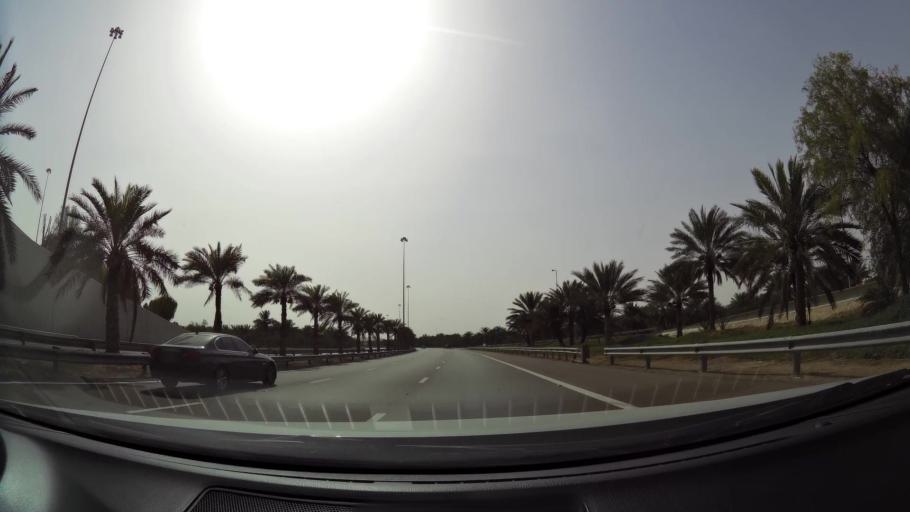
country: AE
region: Abu Dhabi
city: Al Ain
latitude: 24.2003
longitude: 55.5841
